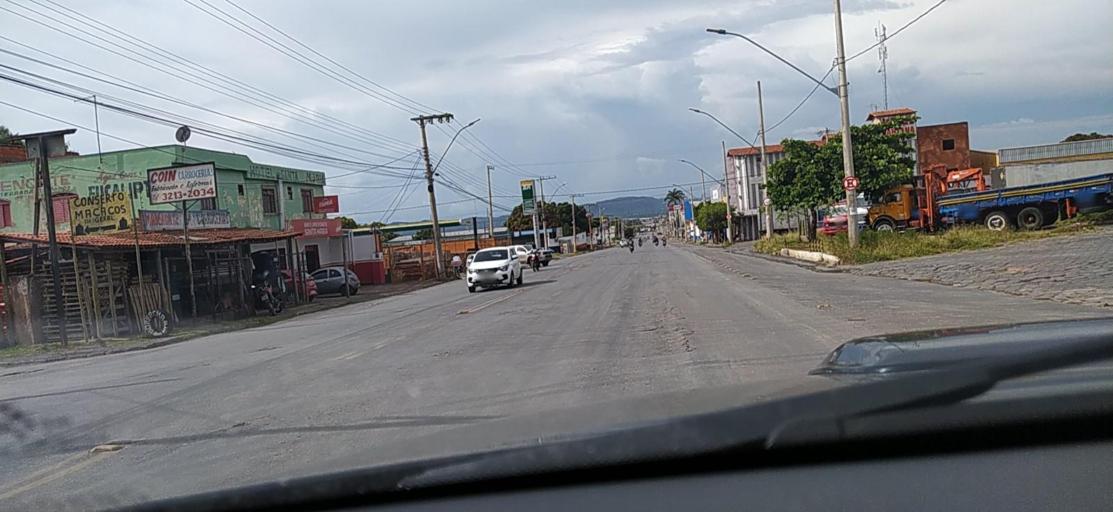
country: BR
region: Minas Gerais
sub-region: Montes Claros
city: Montes Claros
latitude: -16.7407
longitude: -43.8463
